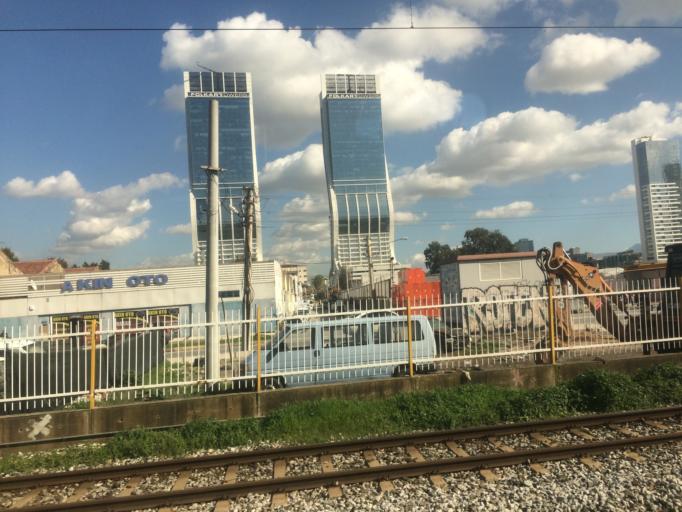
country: TR
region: Izmir
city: Izmir
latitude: 38.4528
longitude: 27.1715
